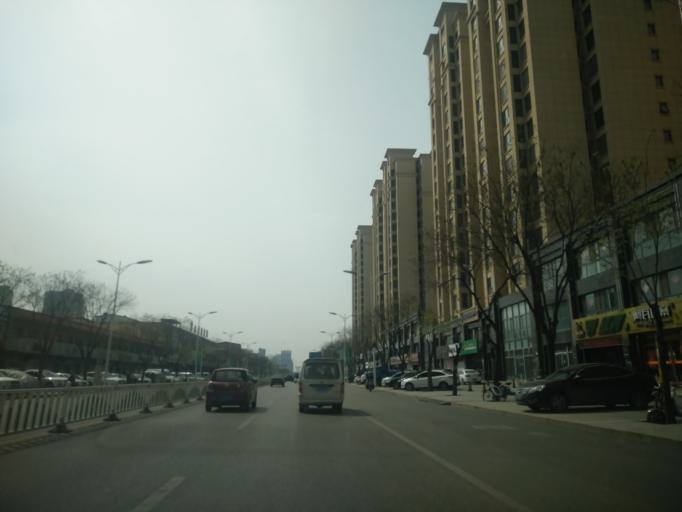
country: CN
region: Beijing
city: Xiji
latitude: 39.7638
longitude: 117.0080
